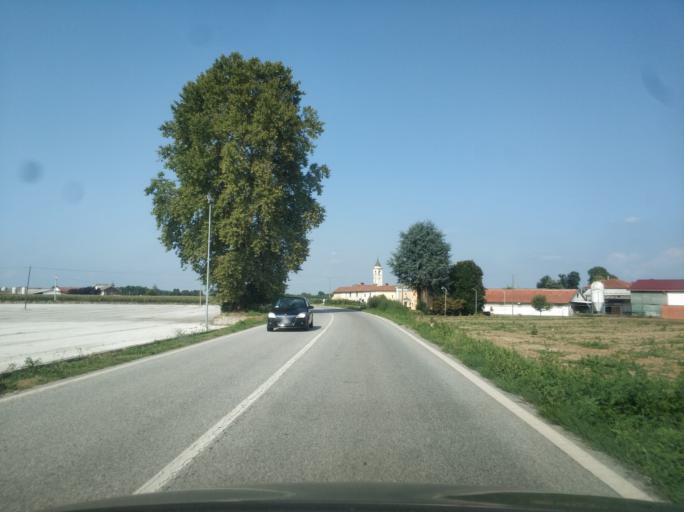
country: IT
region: Piedmont
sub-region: Provincia di Cuneo
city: Centallo
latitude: 44.5154
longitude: 7.5968
